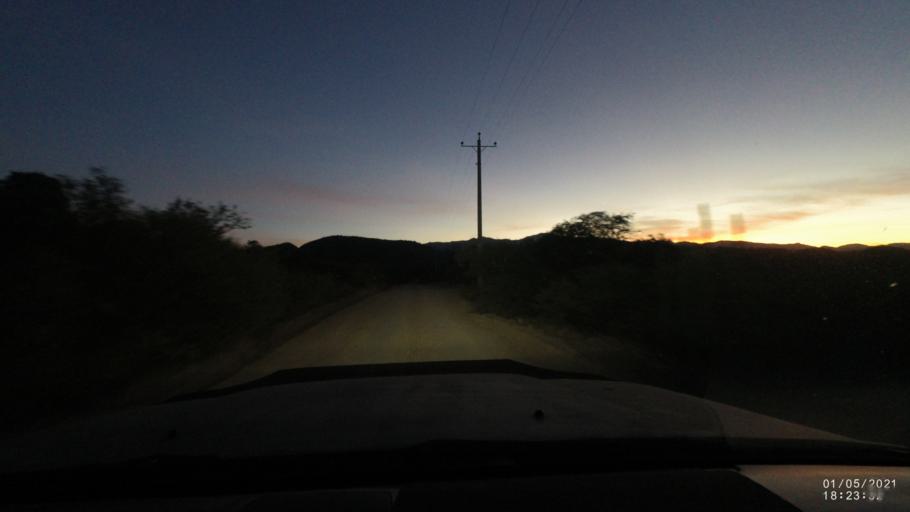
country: BO
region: Cochabamba
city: Capinota
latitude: -17.6581
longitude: -66.2388
